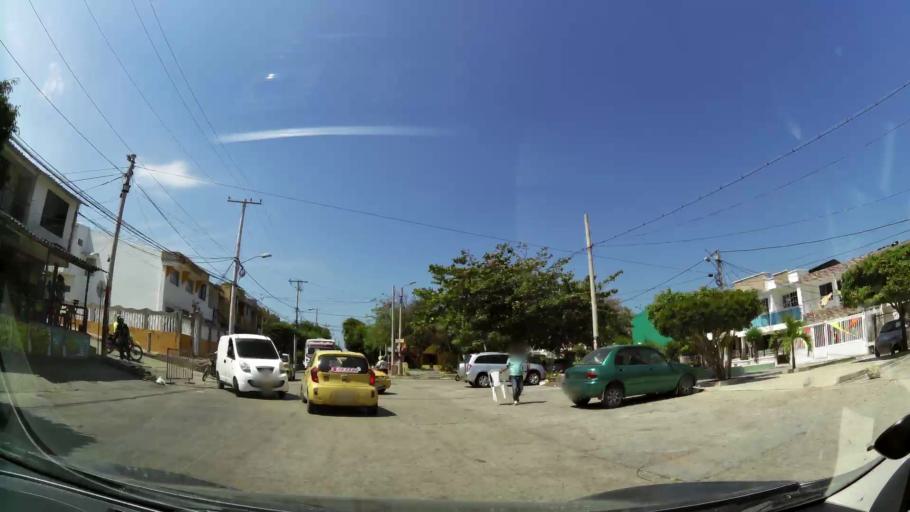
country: CO
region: Atlantico
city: Barranquilla
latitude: 10.9776
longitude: -74.8179
